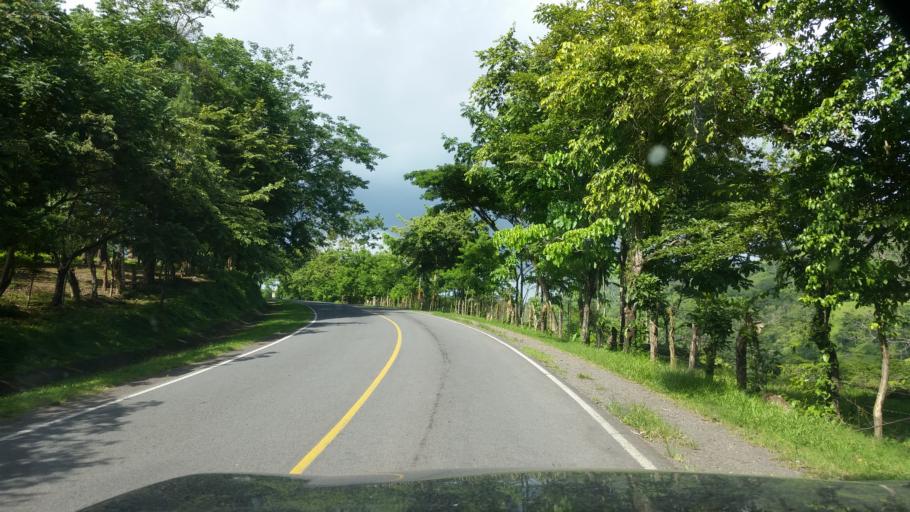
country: NI
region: Matagalpa
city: San Ramon
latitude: 13.0390
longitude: -85.7735
